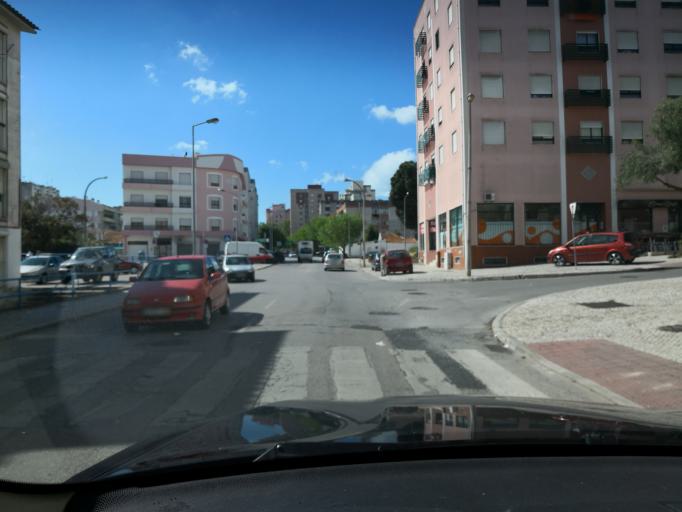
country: PT
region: Setubal
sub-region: Setubal
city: Setubal
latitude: 38.5281
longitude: -8.8704
